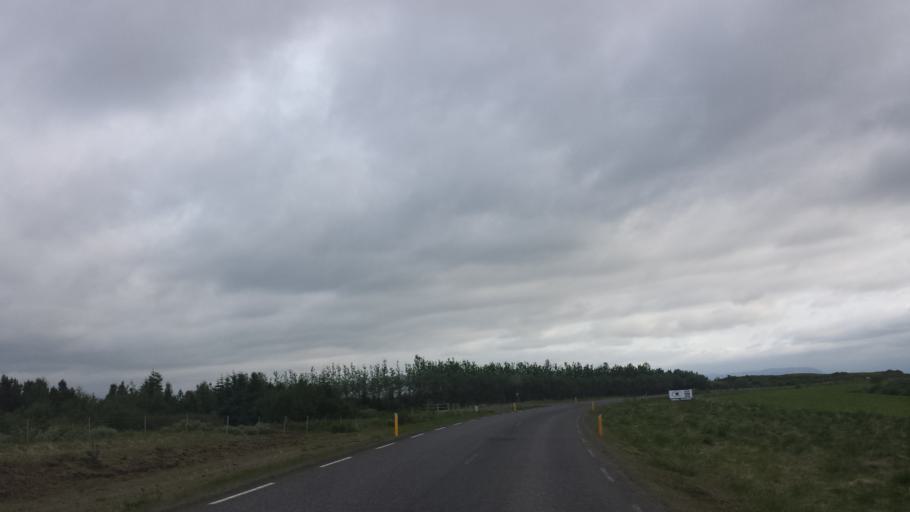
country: IS
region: South
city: Selfoss
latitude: 64.2279
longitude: -20.3394
